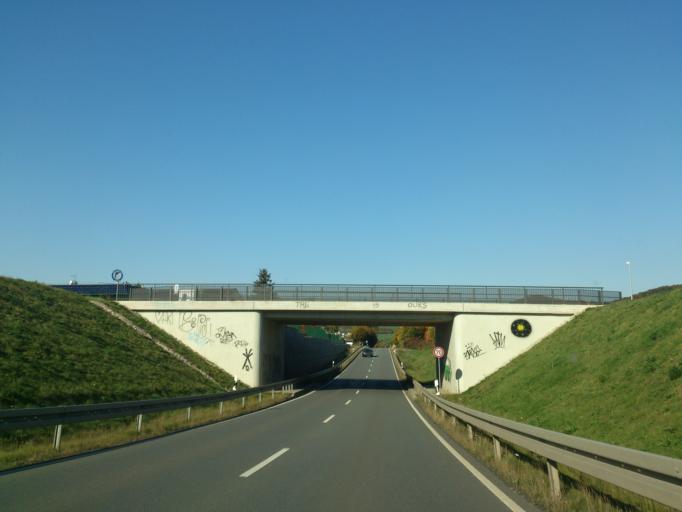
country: DE
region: Hesse
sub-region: Regierungsbezirk Kassel
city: Calden
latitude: 51.3626
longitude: 9.4169
